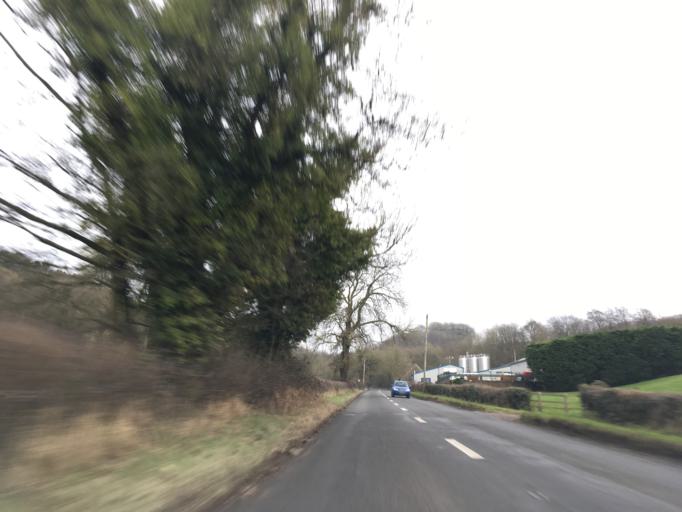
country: GB
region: England
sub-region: South Gloucestershire
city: Hinton
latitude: 51.5017
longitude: -2.3680
